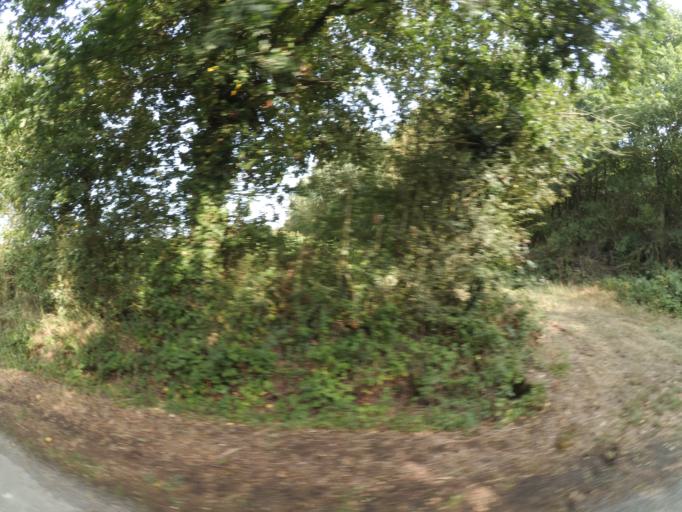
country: FR
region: Pays de la Loire
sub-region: Departement de la Vendee
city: Bouffere
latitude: 46.9418
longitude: -1.3293
